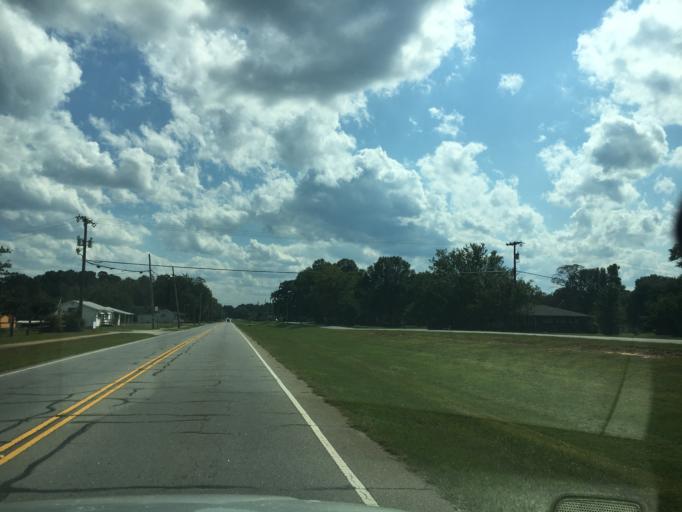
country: US
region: South Carolina
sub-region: Anderson County
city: Belton
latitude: 34.5388
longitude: -82.4950
